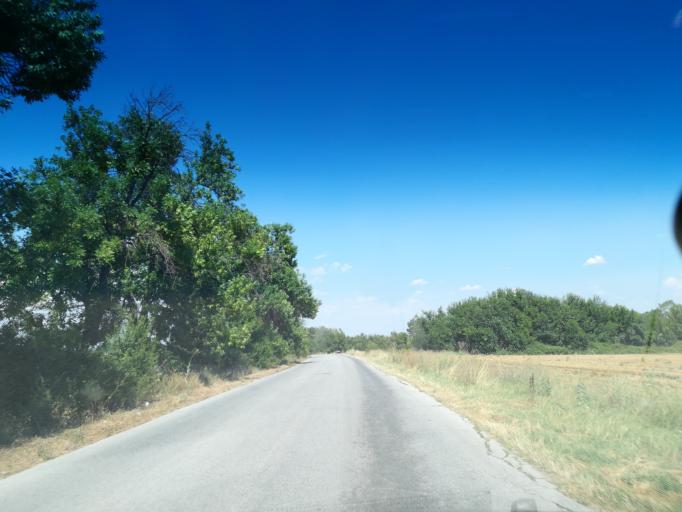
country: BG
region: Stara Zagora
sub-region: Obshtina Chirpan
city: Chirpan
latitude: 42.0662
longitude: 25.1740
